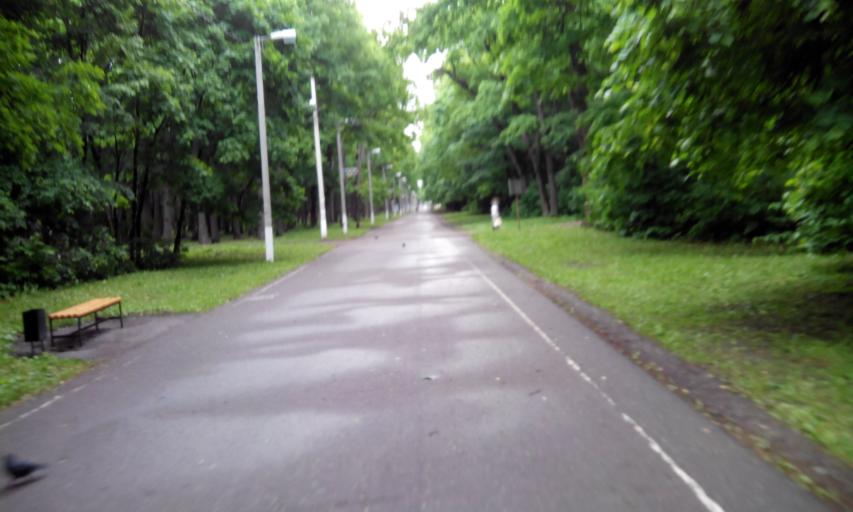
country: RU
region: Penza
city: Penza
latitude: 53.1823
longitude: 44.9826
